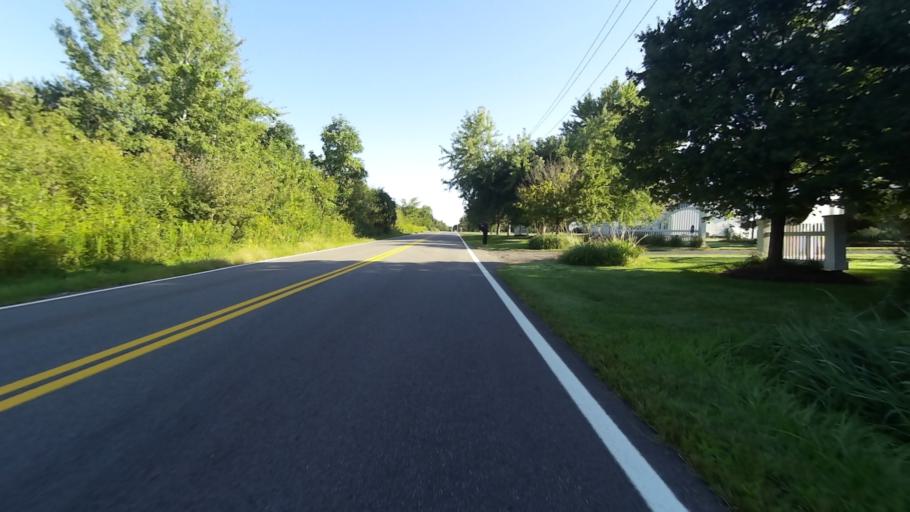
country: US
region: Ohio
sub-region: Portage County
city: Streetsboro
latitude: 41.2768
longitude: -81.3264
